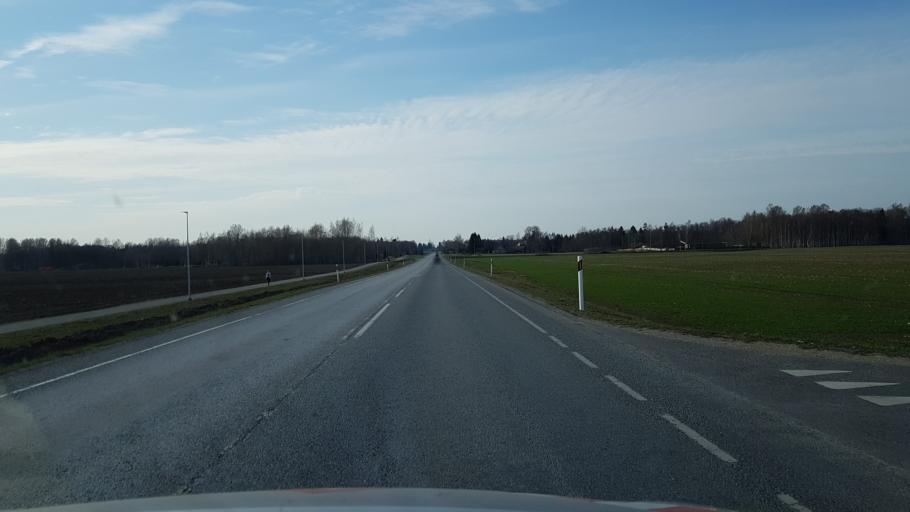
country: EE
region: Laeaene-Virumaa
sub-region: Rakvere linn
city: Rakvere
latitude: 59.3745
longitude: 26.3306
